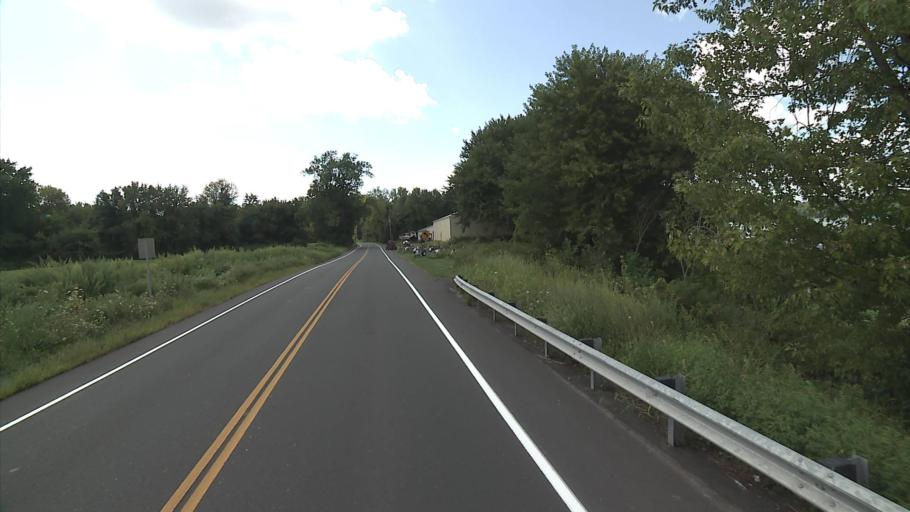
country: US
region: Connecticut
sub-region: Middlesex County
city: Cromwell
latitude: 41.6003
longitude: -72.6178
